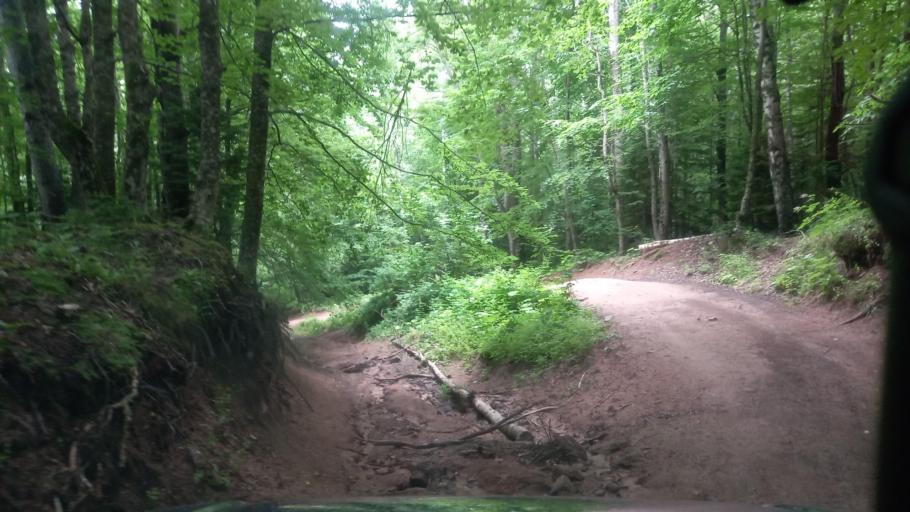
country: RU
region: Karachayevo-Cherkesiya
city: Kurdzhinovo
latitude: 43.8075
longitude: 40.8593
